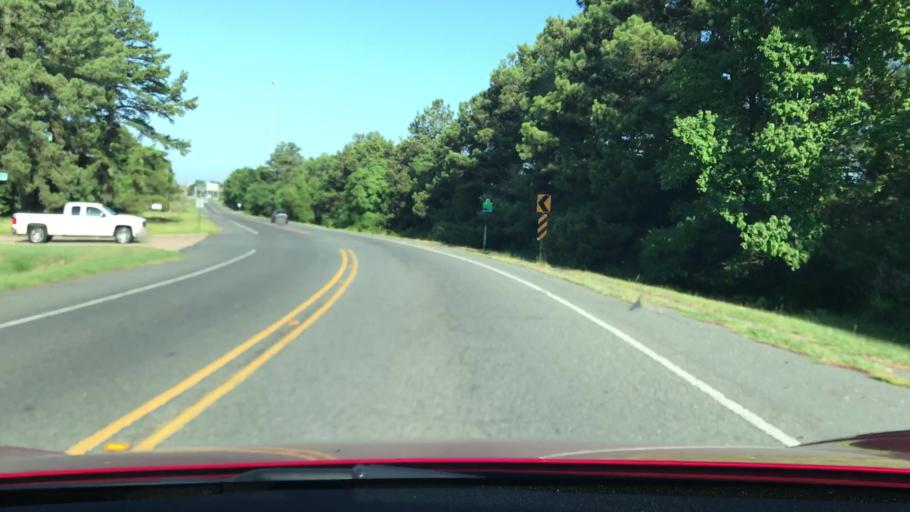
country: US
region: Louisiana
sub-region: Caddo Parish
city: Shreveport
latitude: 32.4541
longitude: -93.8461
